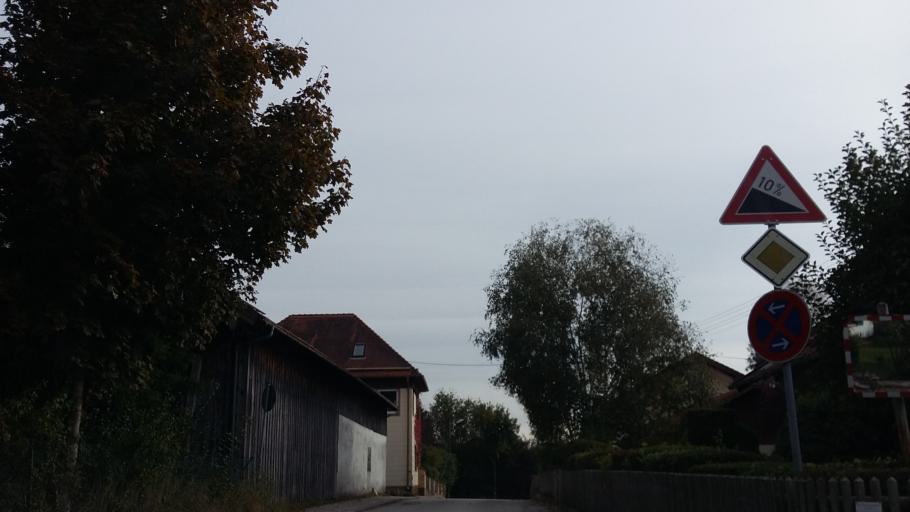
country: DE
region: Bavaria
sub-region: Upper Bavaria
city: Munsing
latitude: 47.9047
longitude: 11.3695
